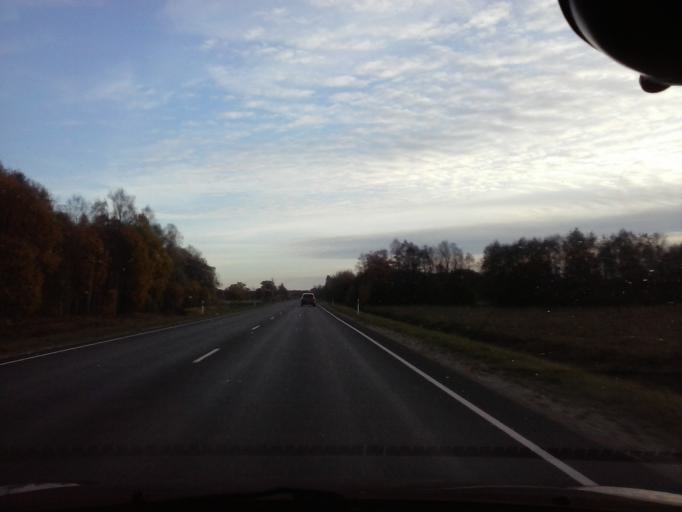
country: EE
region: Harju
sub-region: Nissi vald
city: Turba
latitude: 58.9147
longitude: 24.1119
